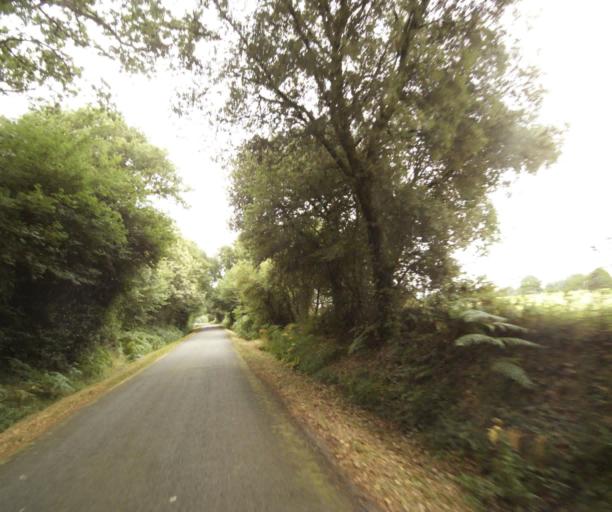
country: FR
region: Pays de la Loire
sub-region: Departement de la Vendee
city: Chateau-d'Olonne
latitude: 46.4931
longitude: -1.6934
